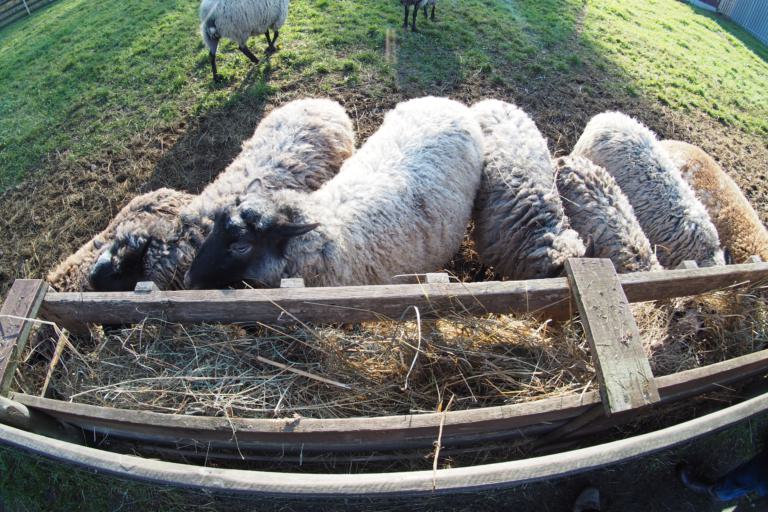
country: RU
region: Moskovskaya
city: Davydovo
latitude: 55.5487
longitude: 38.7992
